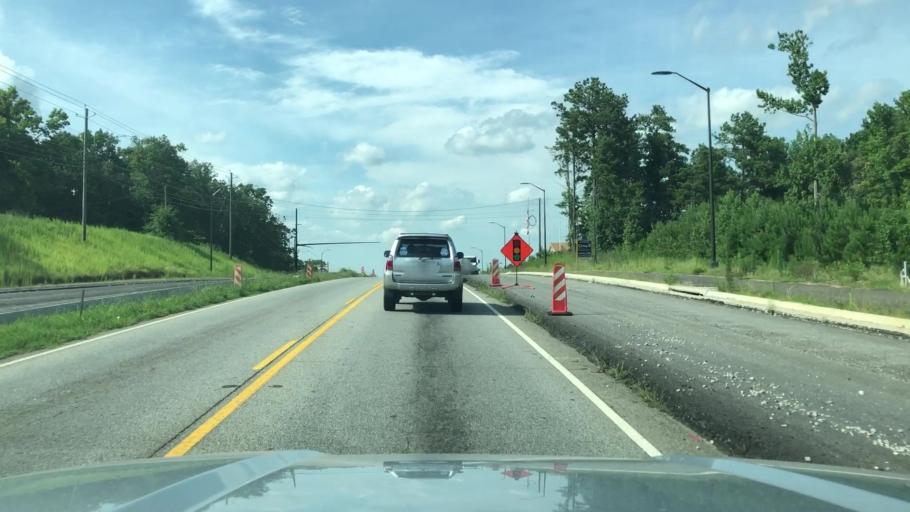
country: US
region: Georgia
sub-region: Douglas County
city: Douglasville
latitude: 33.7664
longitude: -84.7484
